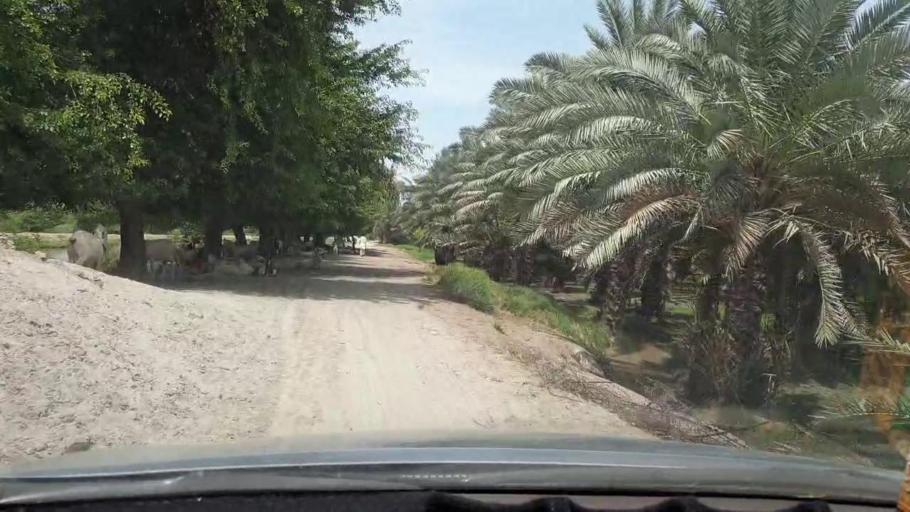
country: PK
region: Sindh
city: Khairpur
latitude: 27.4483
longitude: 68.7970
